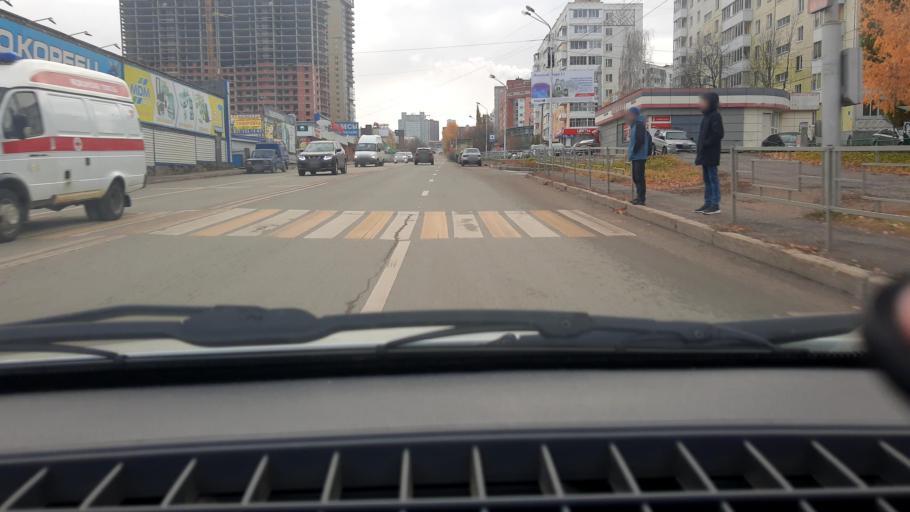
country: RU
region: Bashkortostan
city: Ufa
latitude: 54.7239
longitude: 55.9920
